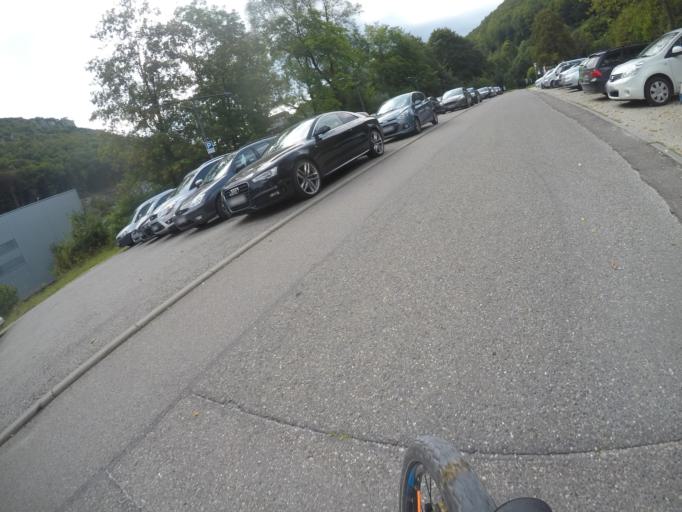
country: DE
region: Baden-Wuerttemberg
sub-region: Tuebingen Region
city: Bad Urach
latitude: 48.4833
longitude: 9.4028
